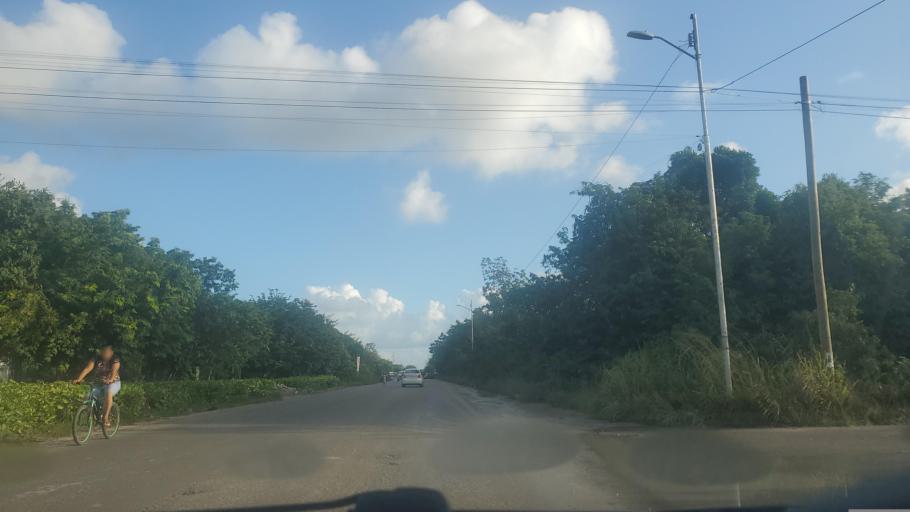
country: MX
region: Quintana Roo
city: Tulum
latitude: 20.2117
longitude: -87.4734
